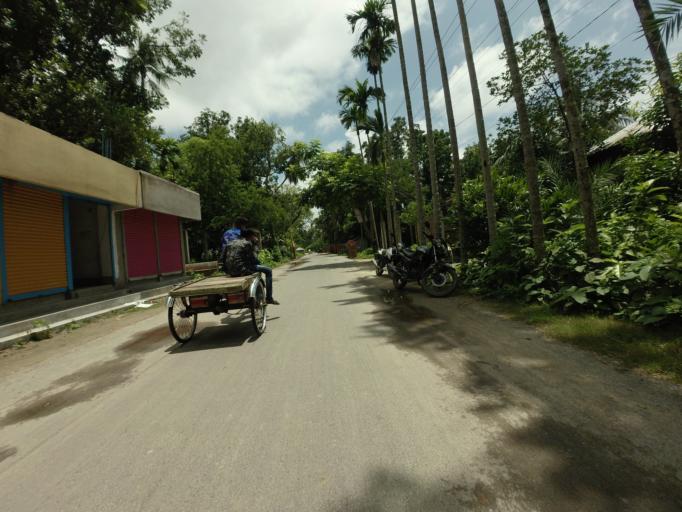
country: BD
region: Khulna
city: Kalia
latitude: 23.0348
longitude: 89.6326
